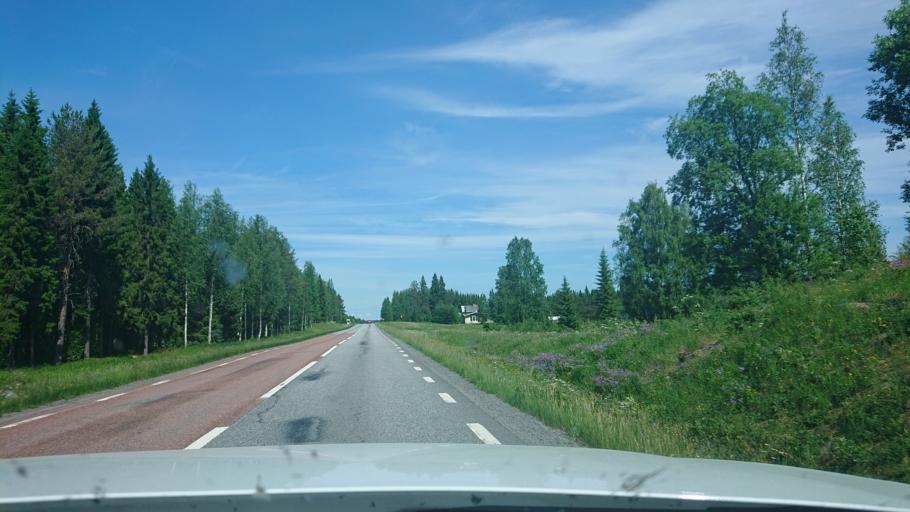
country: SE
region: Jaemtland
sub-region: Stroemsunds Kommun
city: Stroemsund
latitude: 63.7715
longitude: 15.5050
